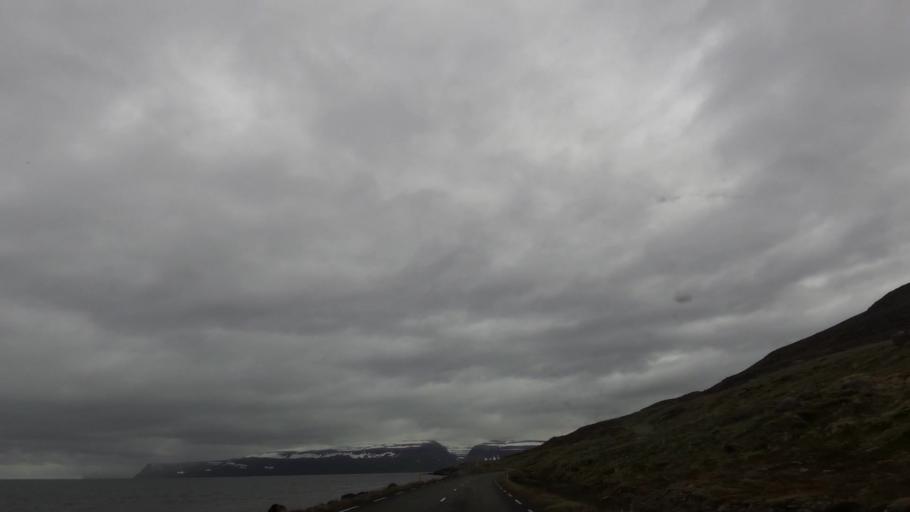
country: IS
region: Westfjords
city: Isafjoerdur
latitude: 66.0377
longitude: -22.7731
